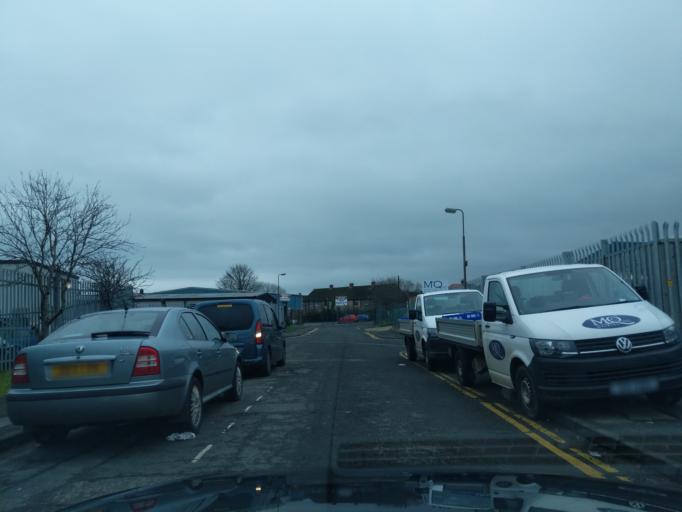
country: GB
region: Scotland
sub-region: Midlothian
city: Loanhead
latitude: 55.8765
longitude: -3.1675
